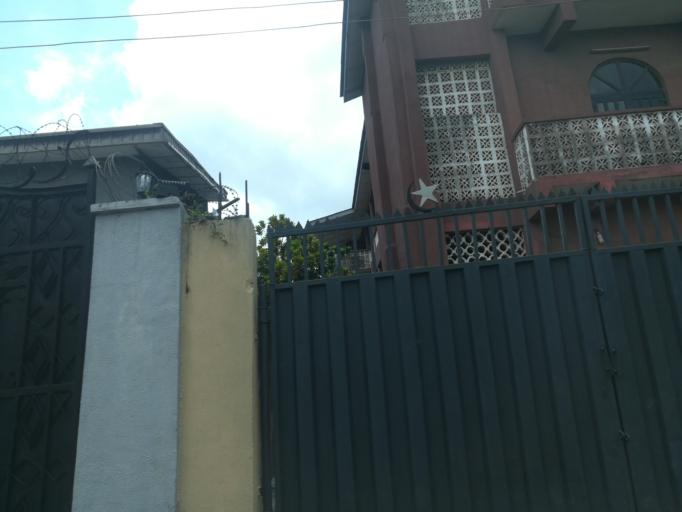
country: NG
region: Lagos
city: Somolu
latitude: 6.5509
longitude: 3.3630
